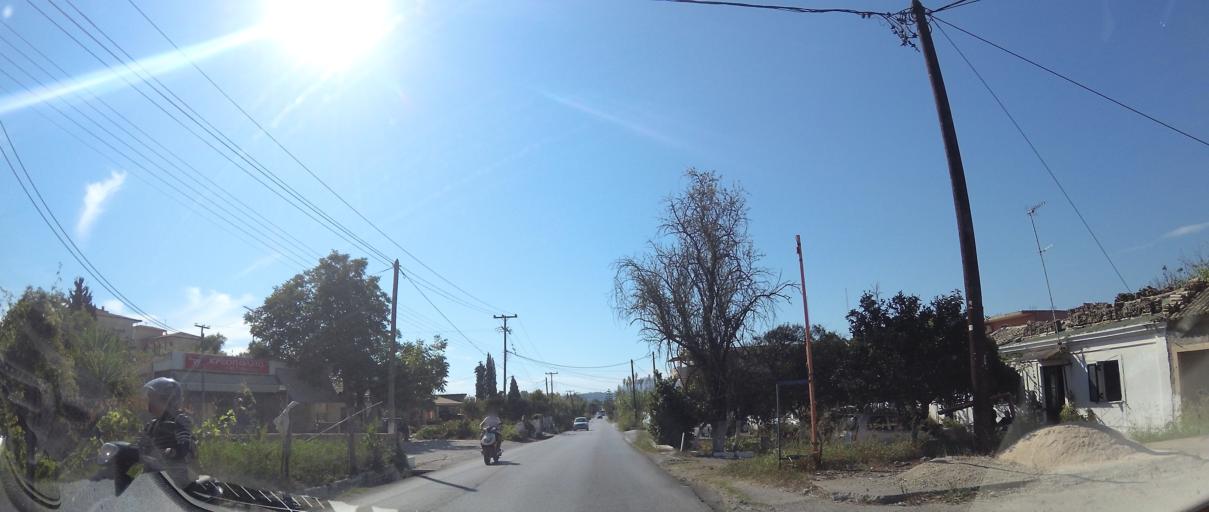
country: GR
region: Ionian Islands
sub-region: Nomos Kerkyras
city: Alepou
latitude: 39.6142
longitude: 19.9035
